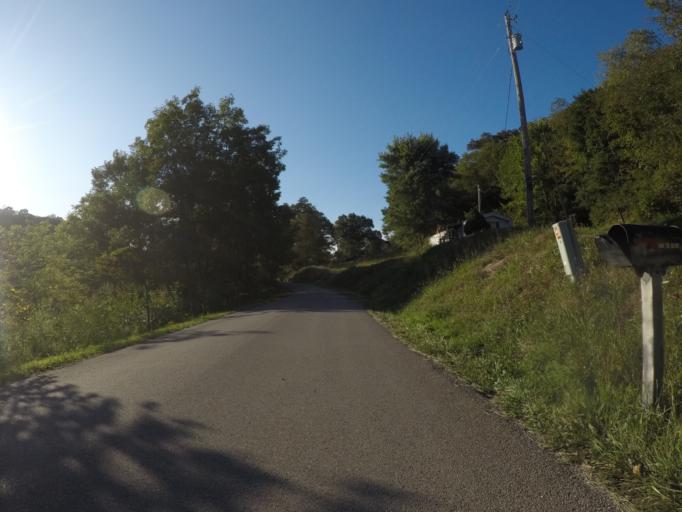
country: US
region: Ohio
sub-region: Lawrence County
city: Coal Grove
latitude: 38.5379
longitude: -82.5467
